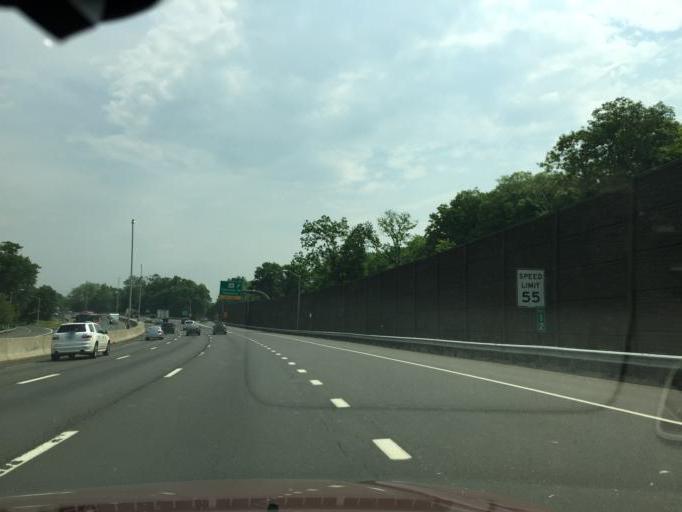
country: US
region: Connecticut
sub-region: Fairfield County
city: Darien
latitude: 41.0744
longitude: -73.4679
